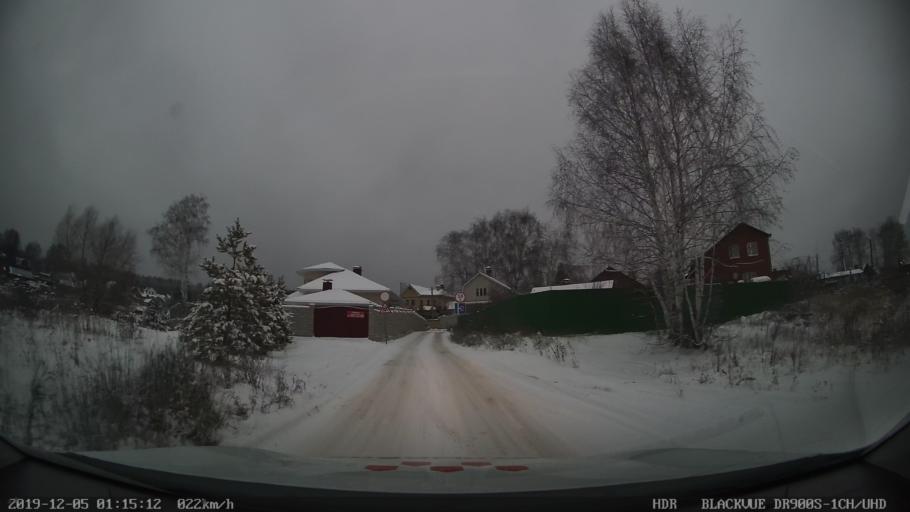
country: RU
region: Tatarstan
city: Stolbishchi
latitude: 55.6453
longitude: 49.1135
